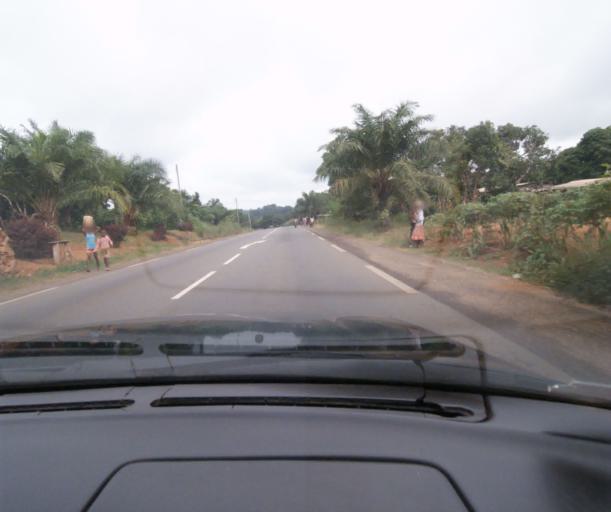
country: CM
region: Centre
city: Obala
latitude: 4.1649
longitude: 11.4982
